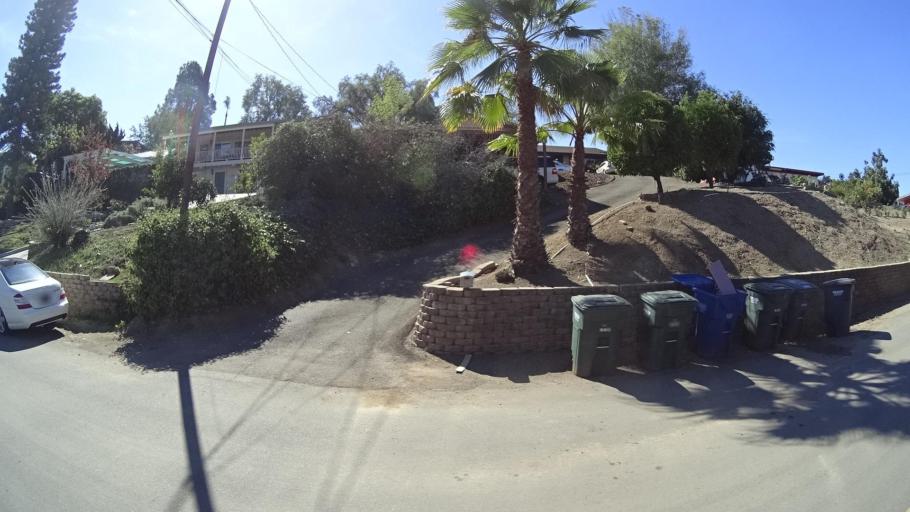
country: US
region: California
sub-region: San Diego County
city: Casa de Oro-Mount Helix
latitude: 32.7494
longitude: -116.9678
